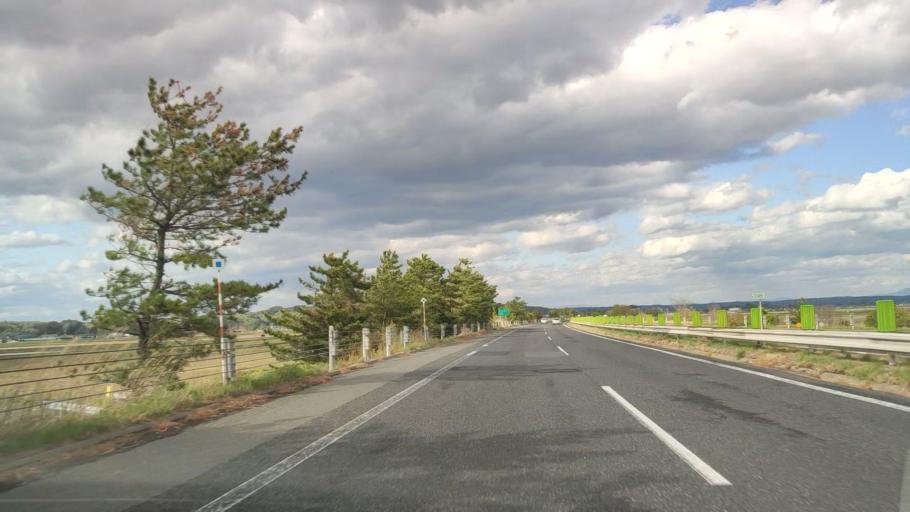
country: JP
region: Iwate
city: Ichinoseki
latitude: 38.7603
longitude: 141.0505
